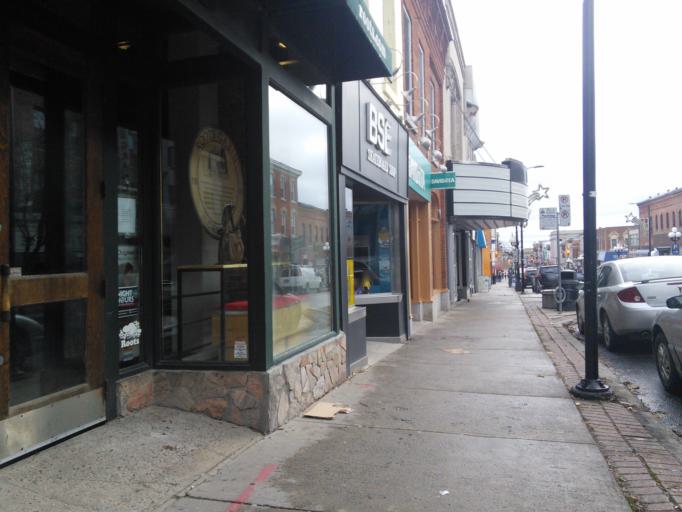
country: CA
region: Ontario
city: Kingston
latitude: 44.2323
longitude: -76.4868
